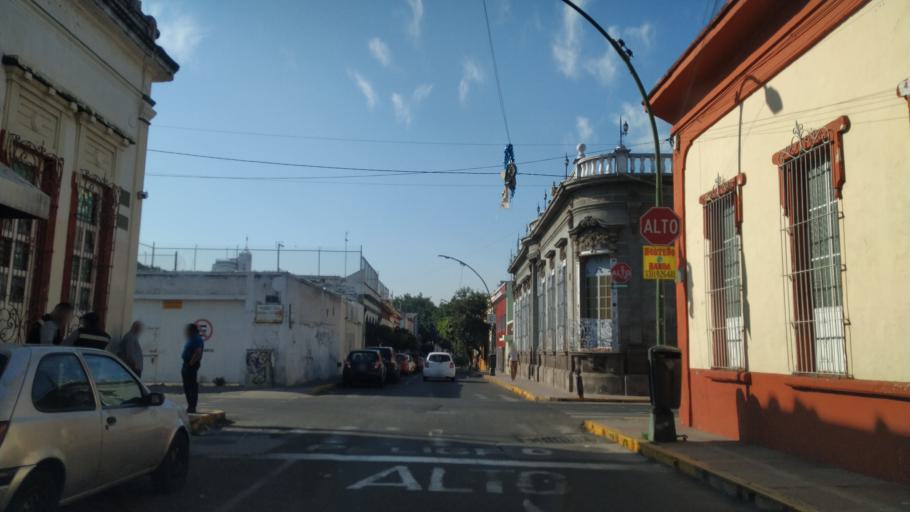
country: MX
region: Jalisco
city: Guadalajara
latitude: 20.6711
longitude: -103.3508
